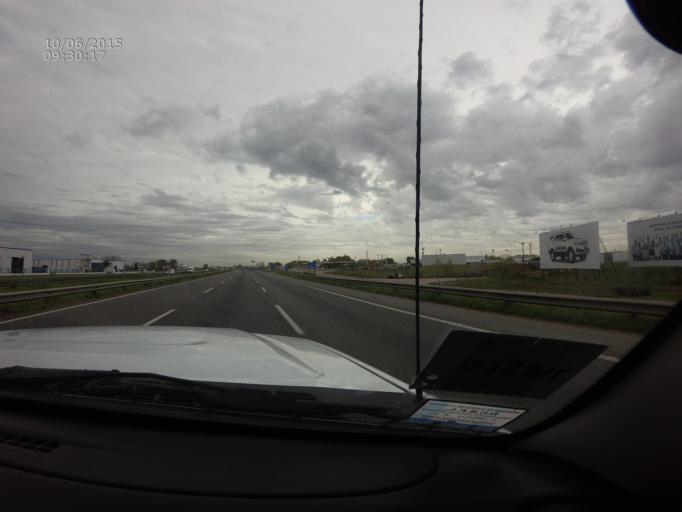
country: AR
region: Buenos Aires
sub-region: Partido de Zarate
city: Zarate
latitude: -34.1425
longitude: -59.0426
